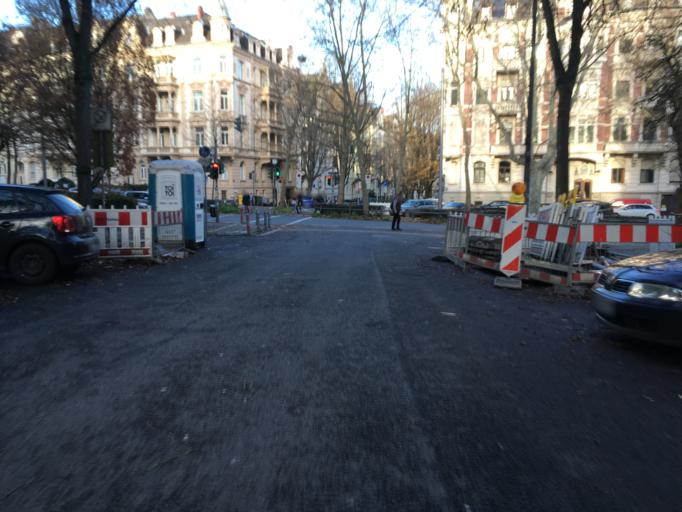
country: DE
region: Hesse
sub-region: Regierungsbezirk Darmstadt
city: Wiesbaden
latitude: 50.0723
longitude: 8.2337
